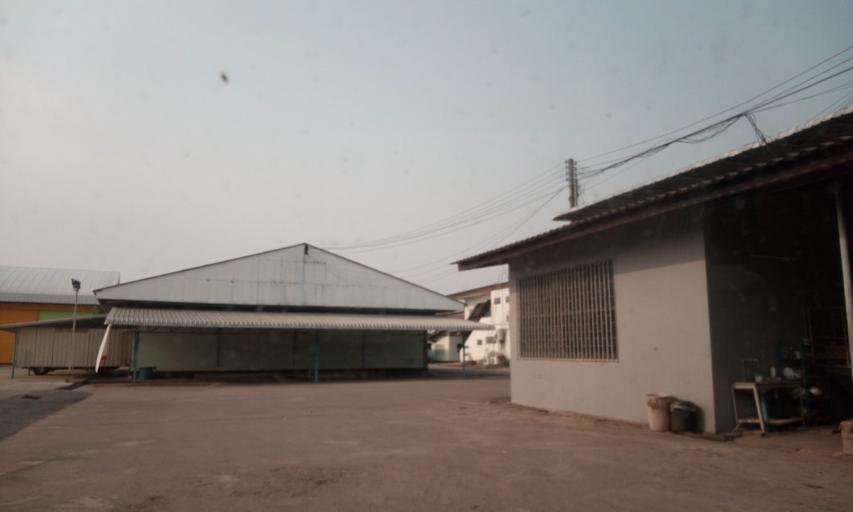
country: TH
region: Chiang Rai
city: Wiang Chai
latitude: 19.7882
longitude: 99.9087
